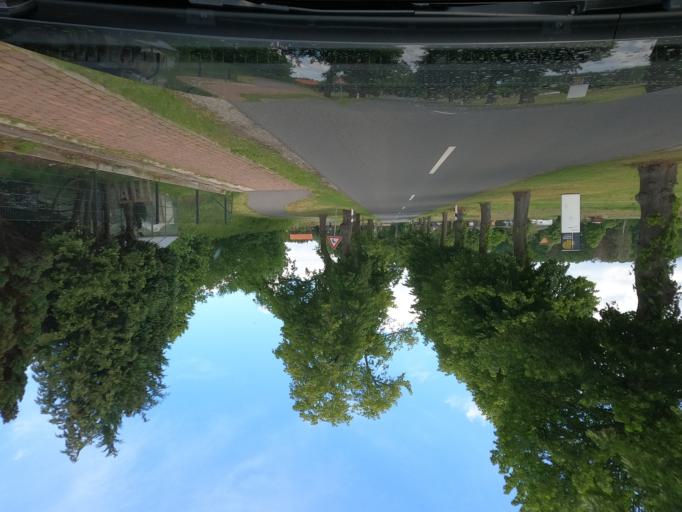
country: DE
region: Lower Saxony
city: Lindwedel
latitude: 52.6325
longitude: 9.6437
